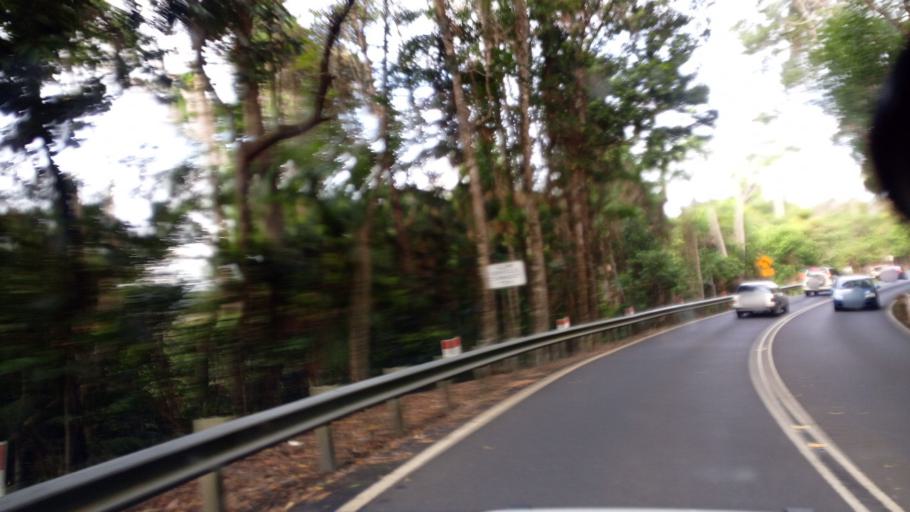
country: AU
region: Queensland
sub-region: Tablelands
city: Kuranda
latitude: -16.8321
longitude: 145.6632
